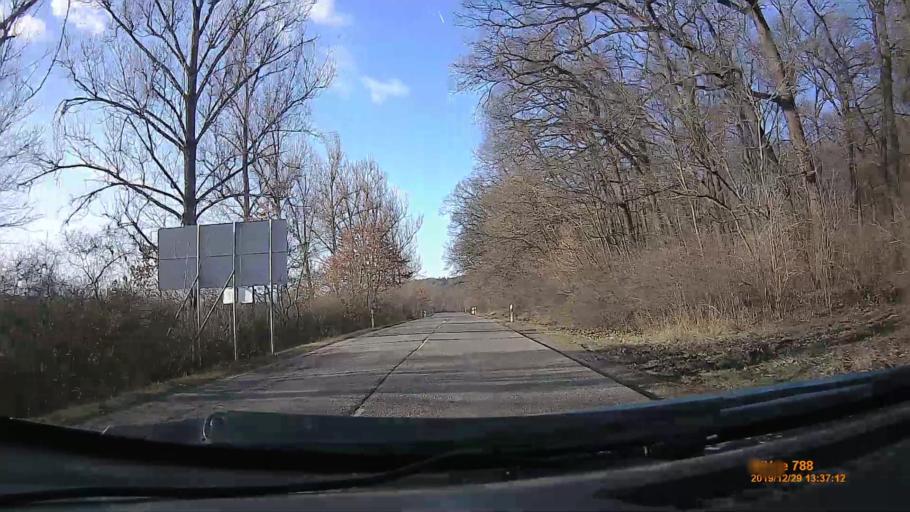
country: HU
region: Heves
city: Sirok
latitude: 47.9217
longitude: 20.1723
